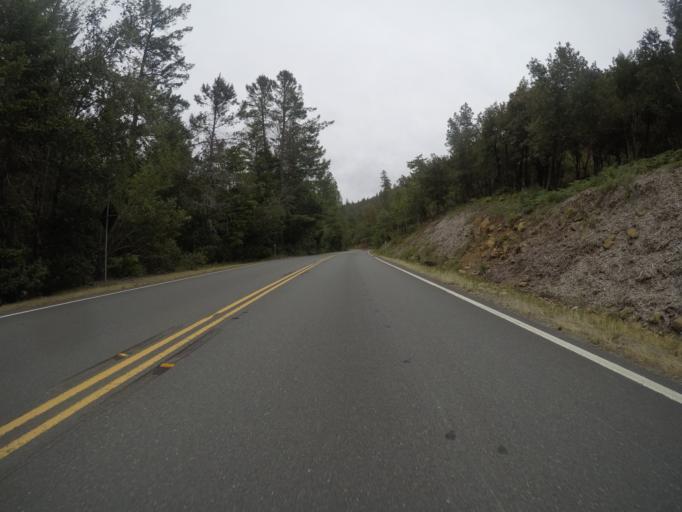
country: US
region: California
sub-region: Del Norte County
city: Bertsch-Oceanview
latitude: 41.7241
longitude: -123.9725
